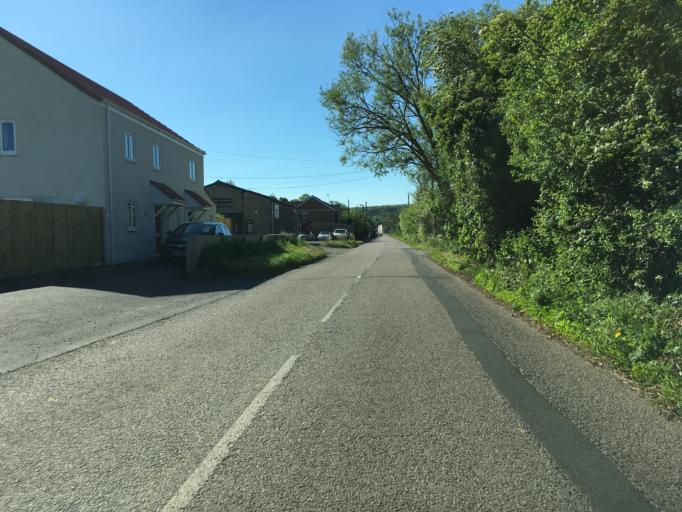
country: GB
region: England
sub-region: South Gloucestershire
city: Severn Beach
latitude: 51.5204
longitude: -2.6514
